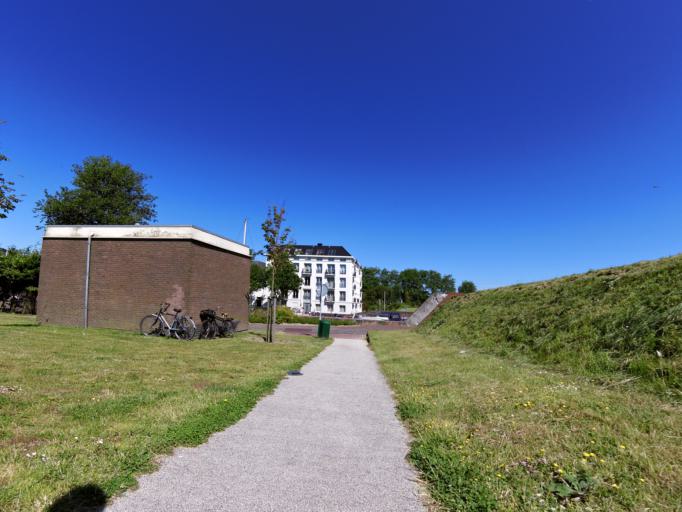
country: NL
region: South Holland
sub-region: Gemeente Hellevoetsluis
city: Hellevoetsluis
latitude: 51.8212
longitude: 4.1276
